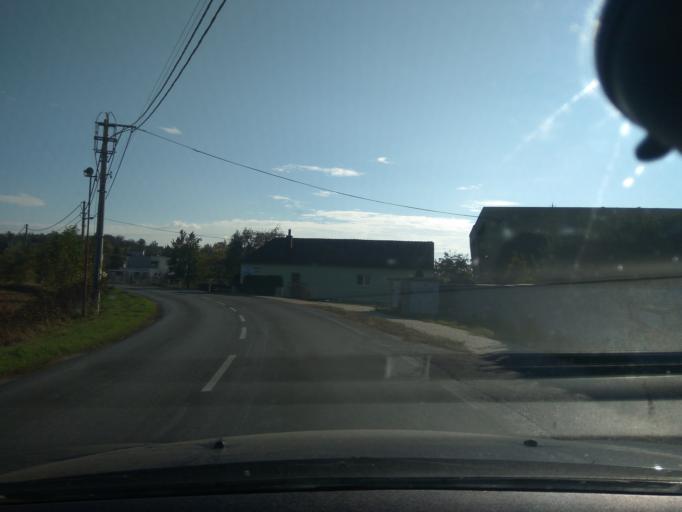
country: SK
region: Trnavsky
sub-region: Okres Trnava
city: Piestany
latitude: 48.5650
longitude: 17.8382
